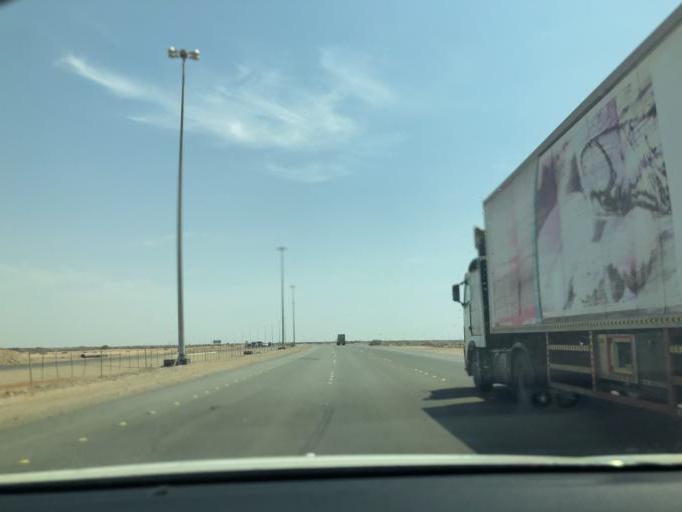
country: SA
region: Makkah
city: Rabigh
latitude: 22.2495
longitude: 39.1151
